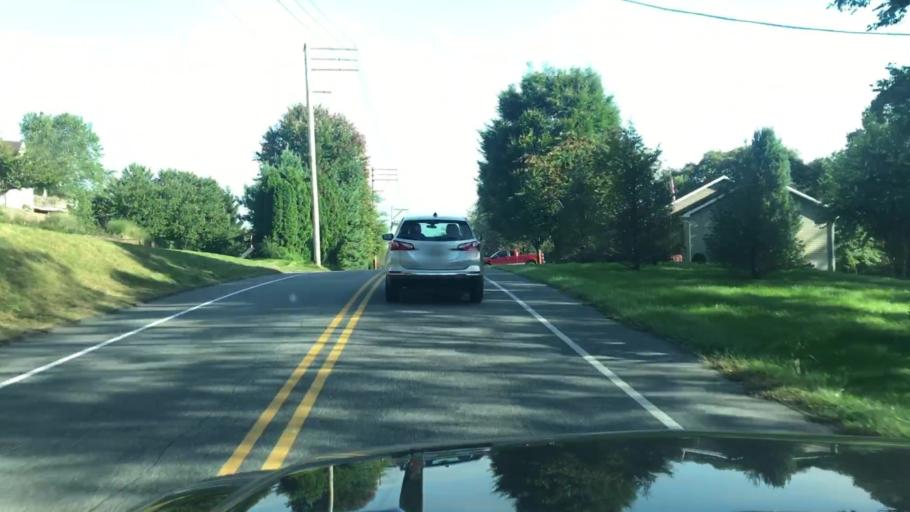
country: US
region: Pennsylvania
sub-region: Cumberland County
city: Shiremanstown
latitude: 40.2674
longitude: -76.9876
